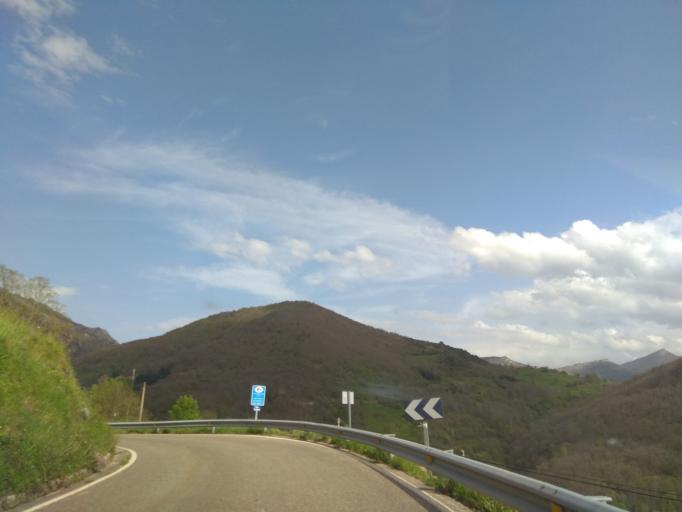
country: ES
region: Cantabria
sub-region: Provincia de Cantabria
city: Tresviso
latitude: 43.2530
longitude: -4.5820
